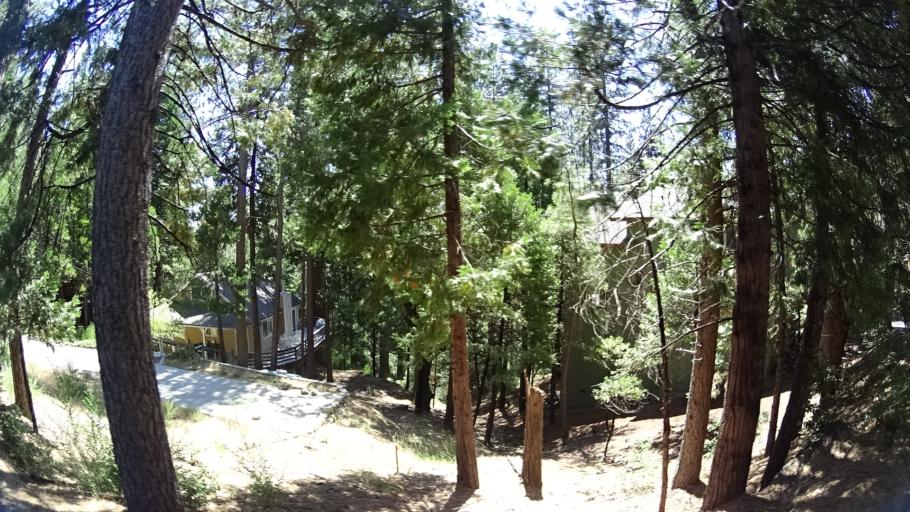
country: US
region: California
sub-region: Calaveras County
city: Arnold
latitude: 38.2303
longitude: -120.3727
